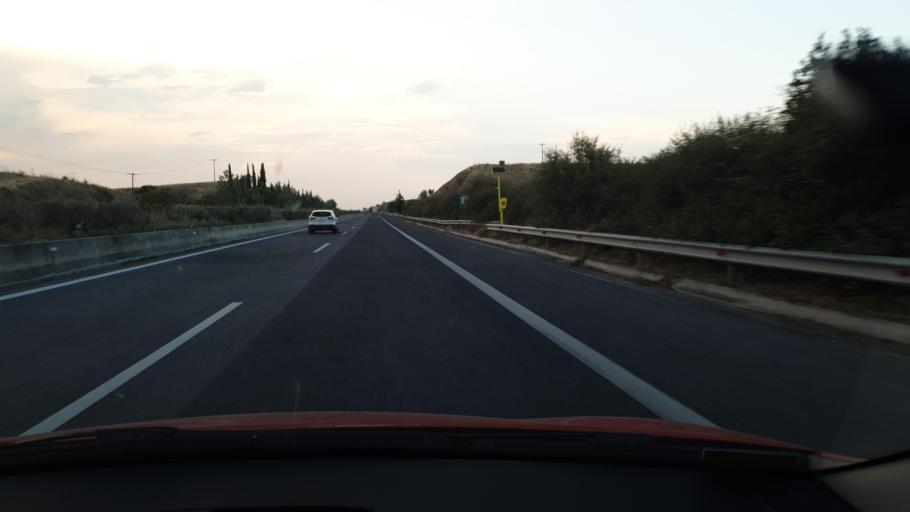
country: GR
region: Thessaly
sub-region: Nomos Magnisias
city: Stefanoviki
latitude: 39.4618
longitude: 22.6704
